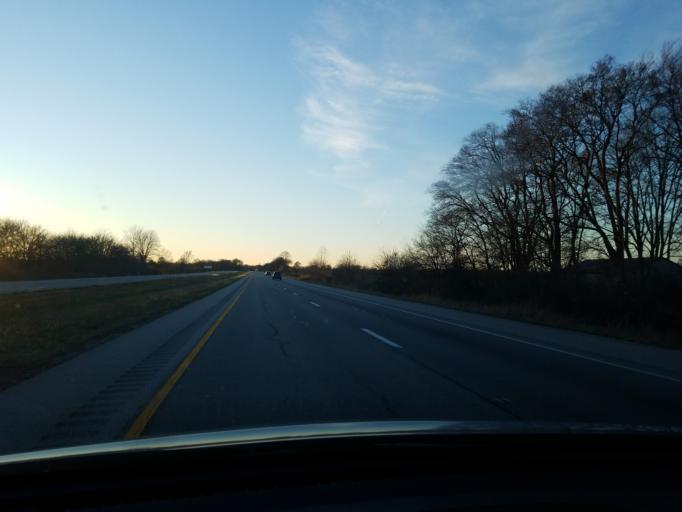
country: US
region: Indiana
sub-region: Posey County
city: Poseyville
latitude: 38.1845
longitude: -87.8091
